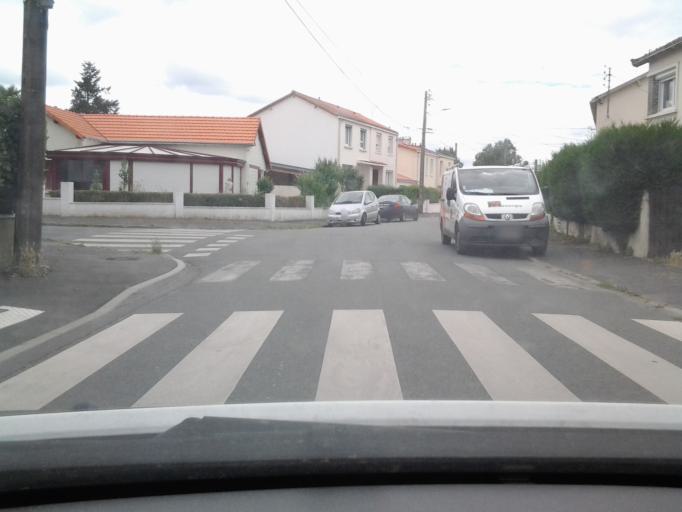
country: FR
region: Pays de la Loire
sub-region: Departement de la Vendee
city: La Roche-sur-Yon
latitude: 46.6601
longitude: -1.4357
